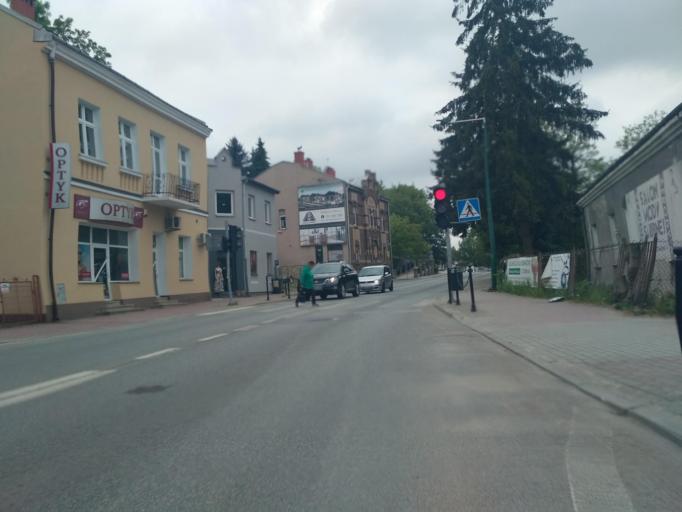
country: PL
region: Subcarpathian Voivodeship
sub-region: Krosno
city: Krosno
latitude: 49.6940
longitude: 21.7629
